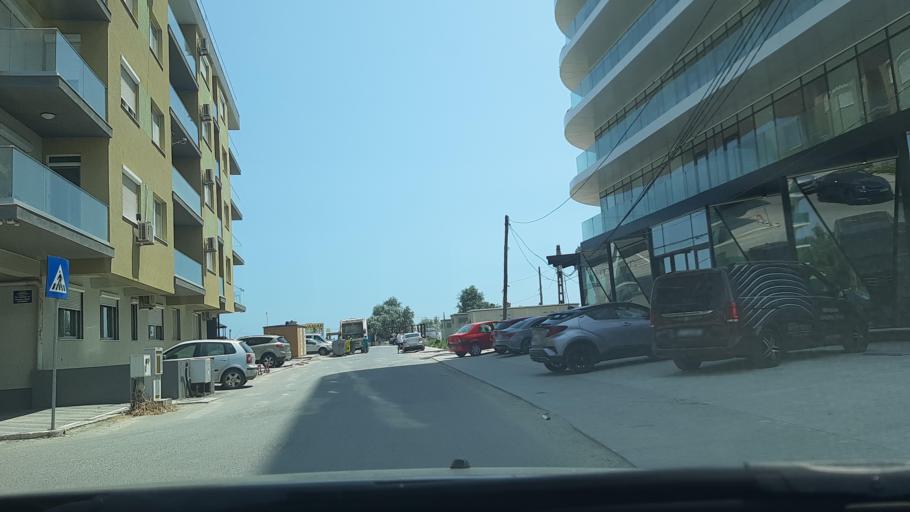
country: RO
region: Constanta
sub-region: Comuna Navodari
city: Navodari
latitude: 44.2881
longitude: 28.6214
